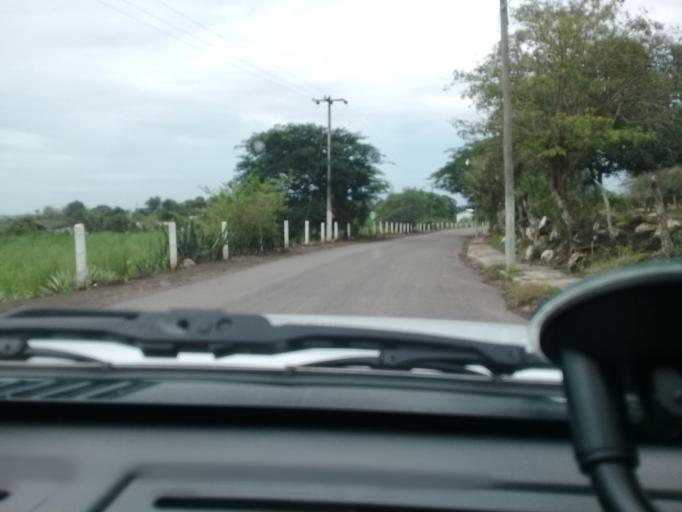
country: MX
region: Veracruz
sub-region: Paso de Ovejas
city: El Hatito
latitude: 19.3115
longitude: -96.3721
